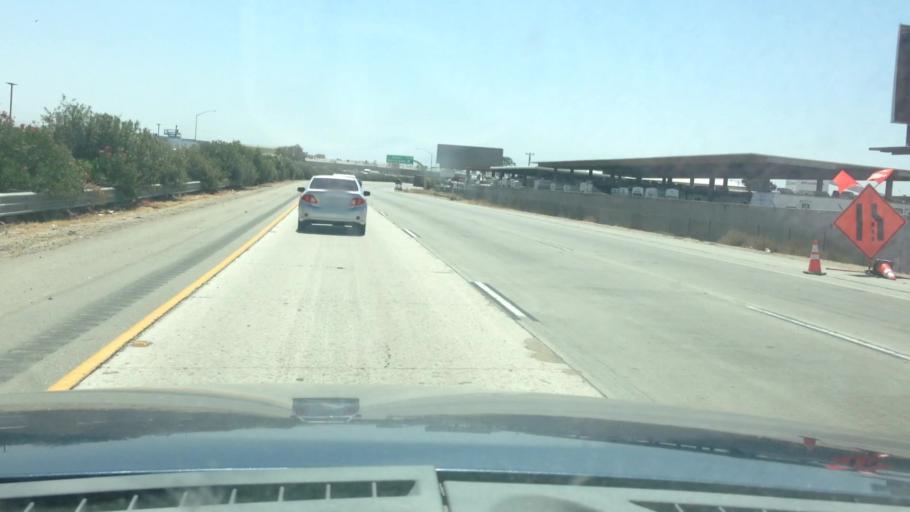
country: US
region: California
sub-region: Kern County
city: Oildale
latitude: 35.4267
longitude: -119.0668
